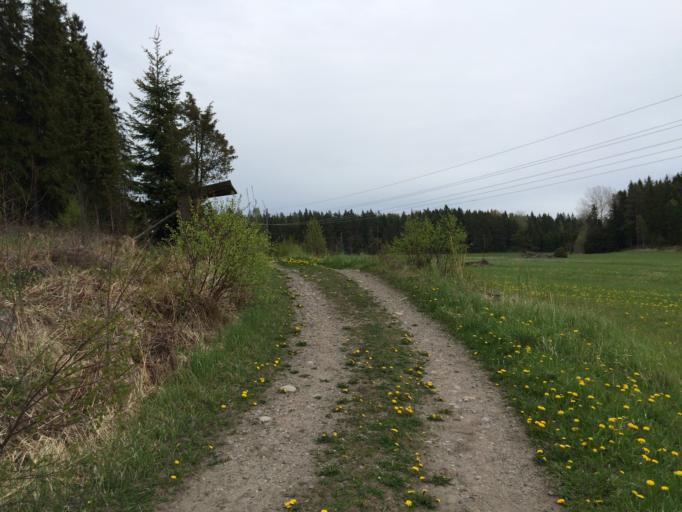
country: SE
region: Stockholm
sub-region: Norrtalje Kommun
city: Norrtalje
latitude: 59.6543
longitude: 18.6572
